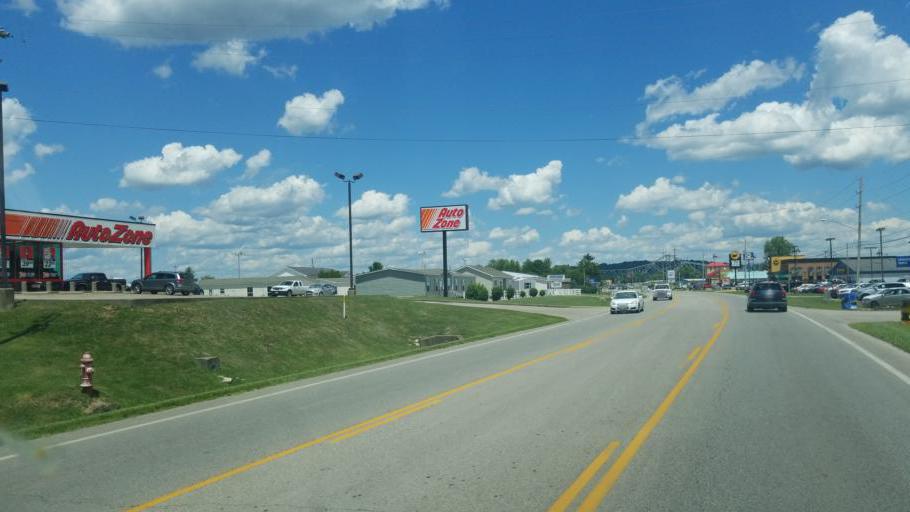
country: US
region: West Virginia
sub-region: Mason County
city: Point Pleasant
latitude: 38.8296
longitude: -82.1616
